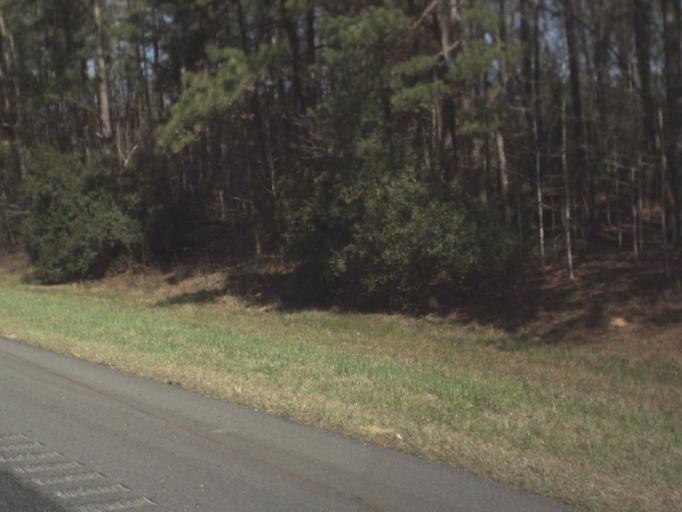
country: US
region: Florida
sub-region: Gadsden County
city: Chattahoochee
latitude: 30.6199
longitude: -84.8356
